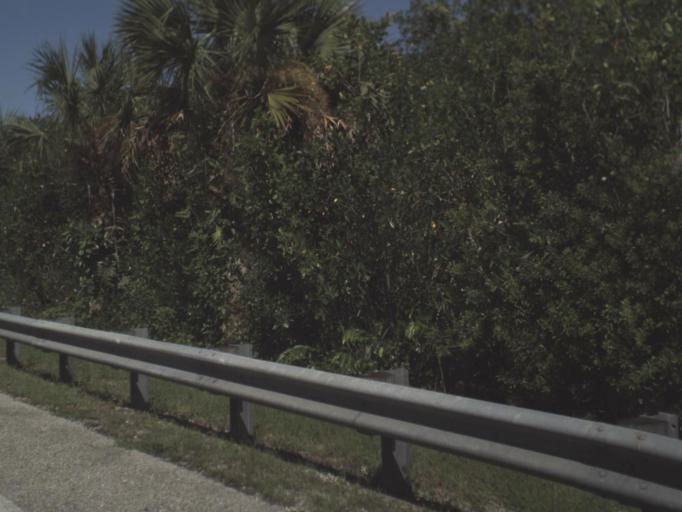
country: US
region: Florida
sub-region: Collier County
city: Marco
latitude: 25.9128
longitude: -81.3691
